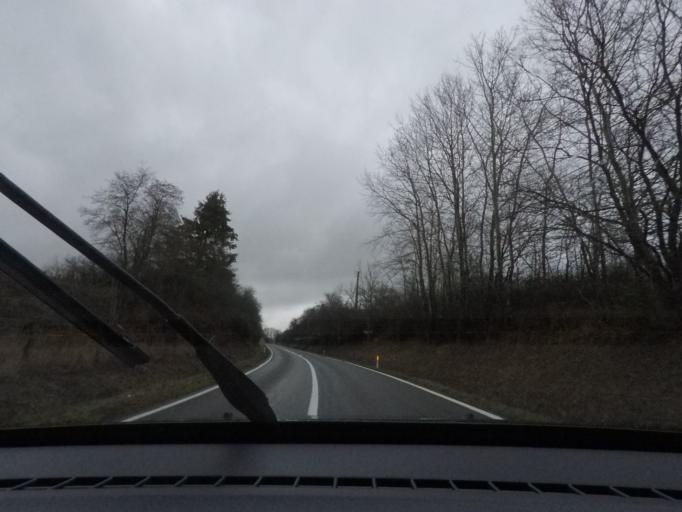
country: BE
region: Wallonia
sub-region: Province du Luxembourg
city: Tintigny
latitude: 49.6969
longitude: 5.5285
